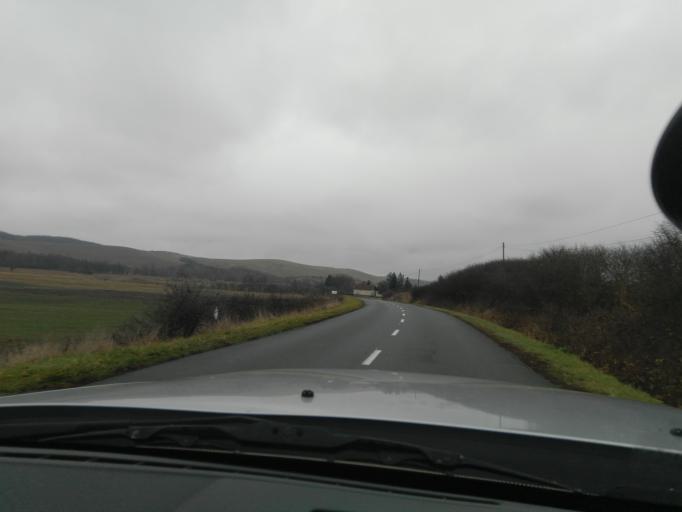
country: HU
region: Nograd
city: Matraterenye
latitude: 48.0413
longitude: 19.9354
